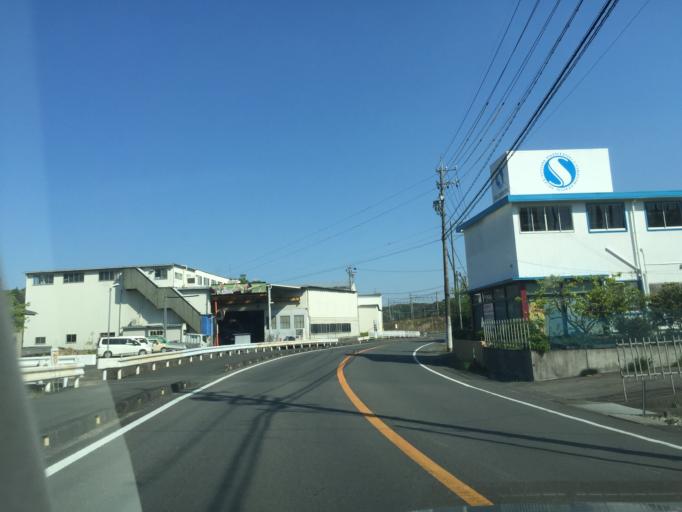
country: JP
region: Shizuoka
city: Kakegawa
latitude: 34.7769
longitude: 138.0387
